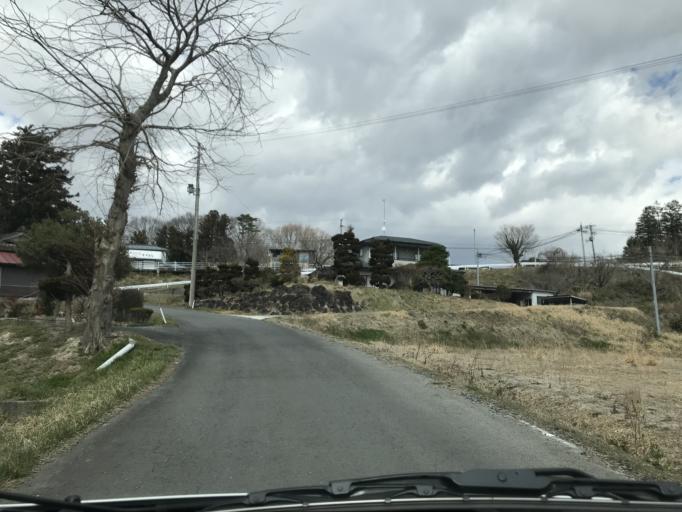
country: JP
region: Miyagi
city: Wakuya
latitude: 38.6919
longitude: 141.1447
